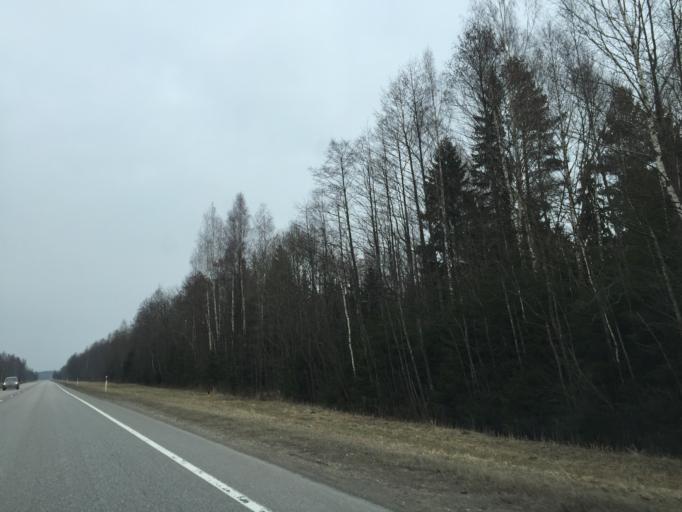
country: LV
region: Salacgrivas
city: Ainazi
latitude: 58.0633
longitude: 24.5114
